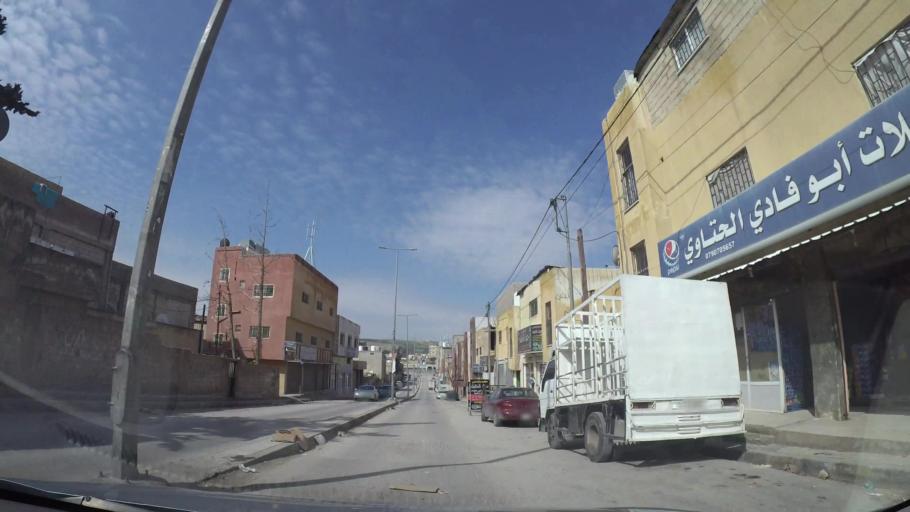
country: JO
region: Amman
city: Al Jubayhah
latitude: 32.0780
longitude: 35.8412
